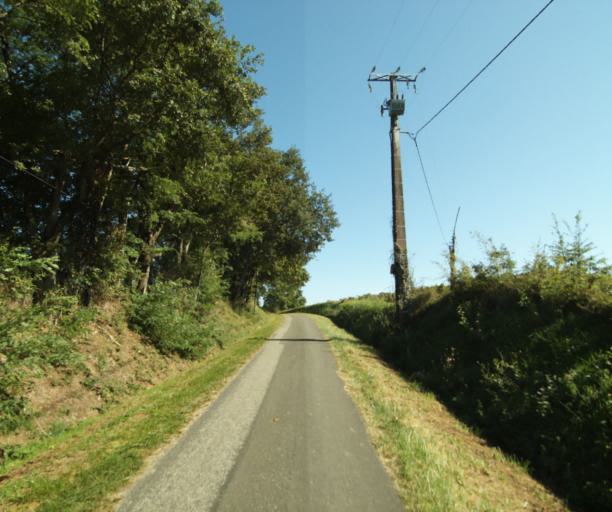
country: FR
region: Midi-Pyrenees
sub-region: Departement du Gers
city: Cazaubon
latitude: 43.9394
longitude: -0.0371
